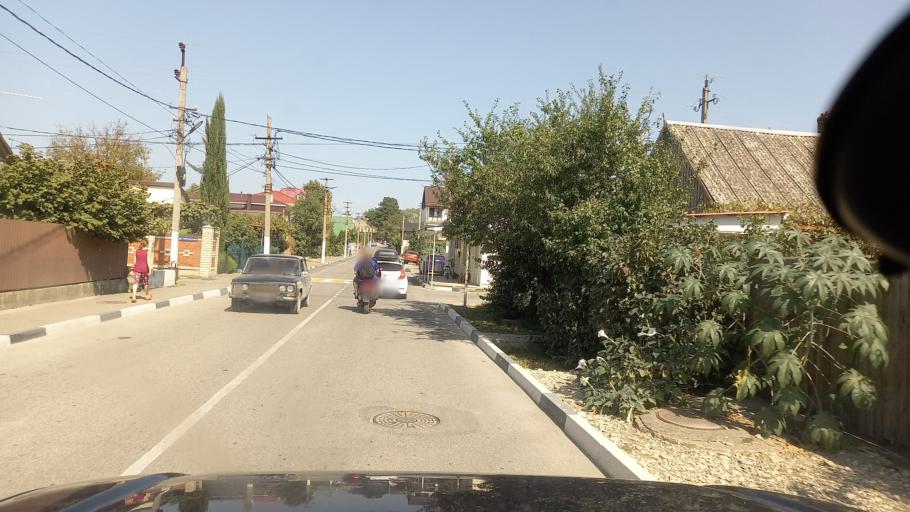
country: RU
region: Krasnodarskiy
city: Arkhipo-Osipovka
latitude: 44.3681
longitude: 38.5321
